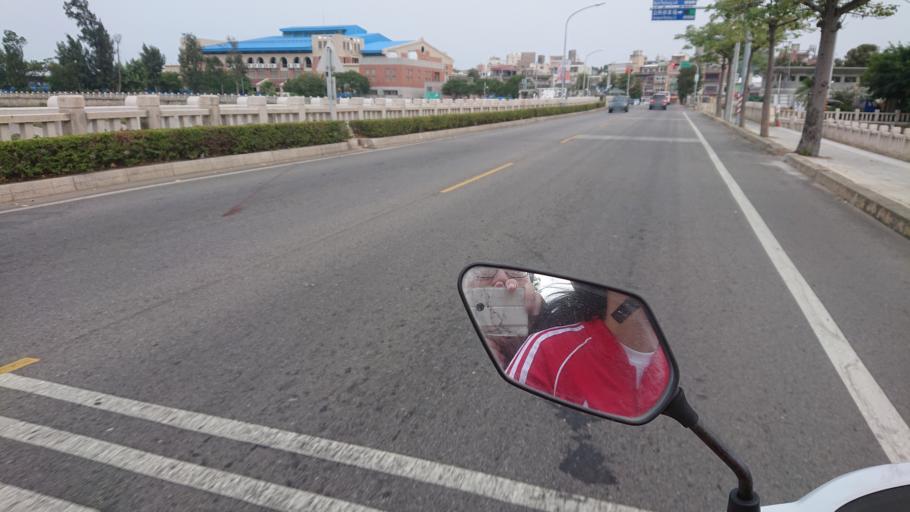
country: TW
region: Fukien
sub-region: Kinmen
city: Jincheng
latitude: 24.4283
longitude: 118.3156
